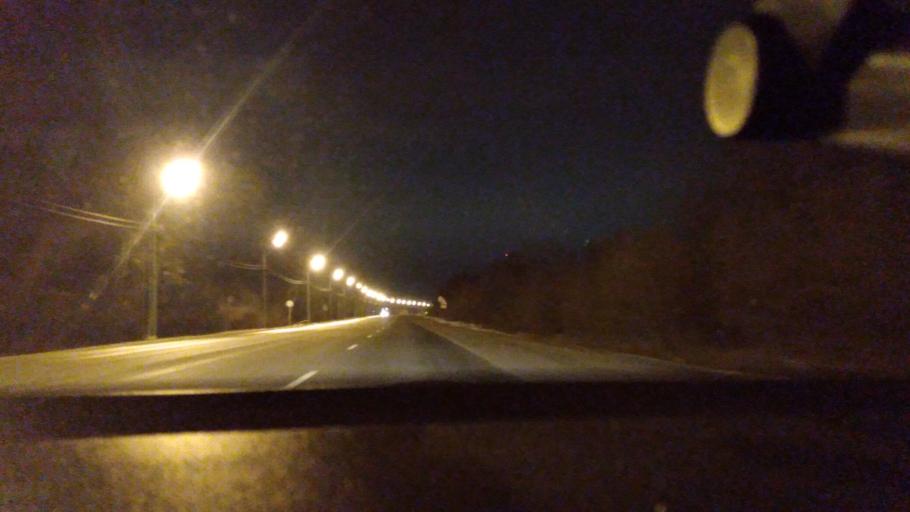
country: RU
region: Moskovskaya
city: Bronnitsy
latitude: 55.3889
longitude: 38.3360
